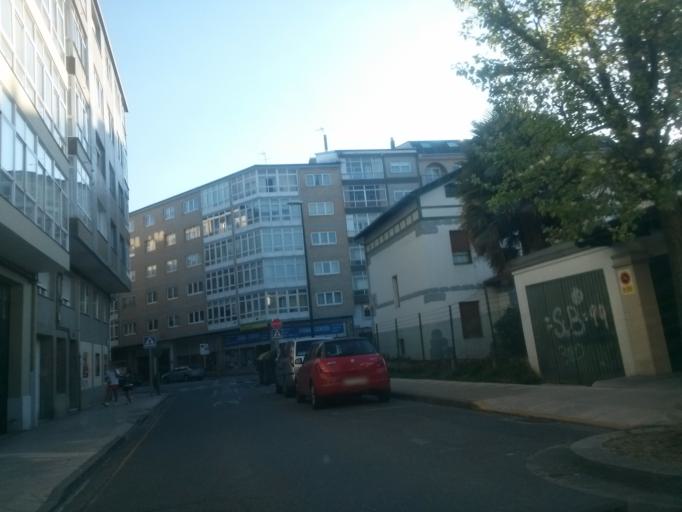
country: ES
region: Galicia
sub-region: Provincia de Lugo
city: Lugo
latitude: 43.0140
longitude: -7.5623
